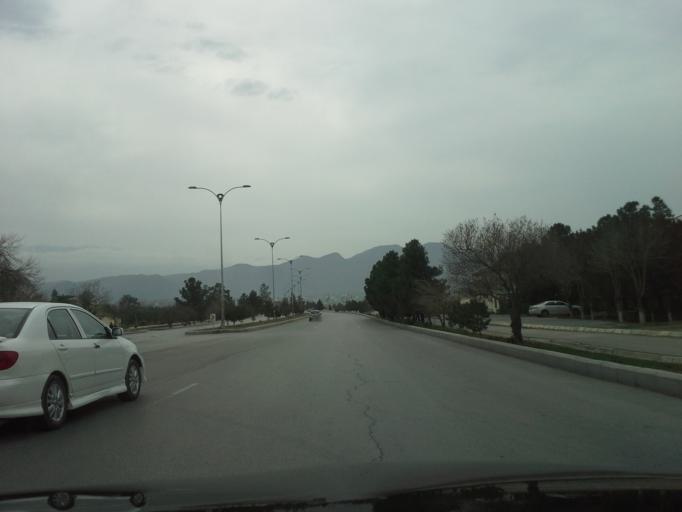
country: TM
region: Ahal
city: Abadan
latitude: 37.9702
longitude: 58.2333
